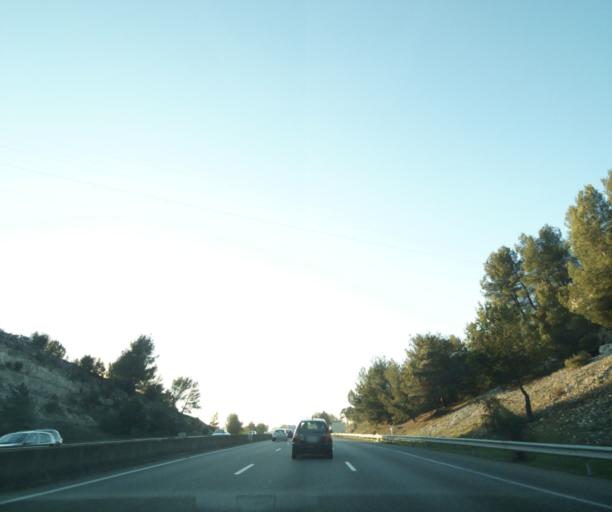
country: FR
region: Provence-Alpes-Cote d'Azur
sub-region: Departement des Bouches-du-Rhone
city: Aix-en-Provence
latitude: 43.5133
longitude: 5.4762
